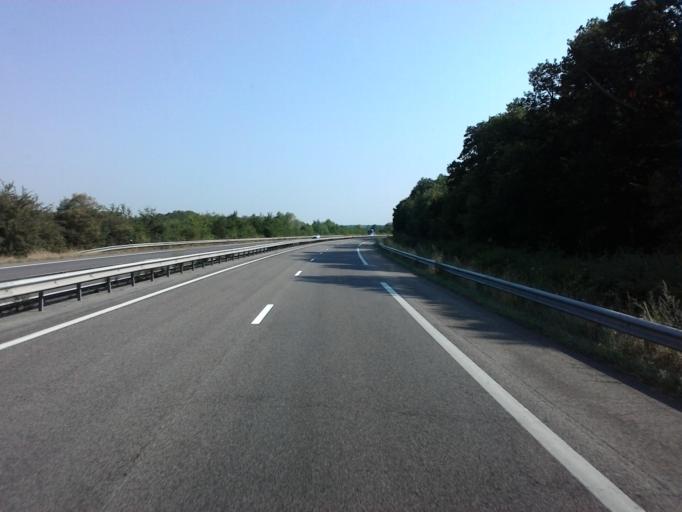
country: FR
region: Lorraine
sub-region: Departement de Meurthe-et-Moselle
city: Bayon
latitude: 48.4536
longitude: 6.2351
